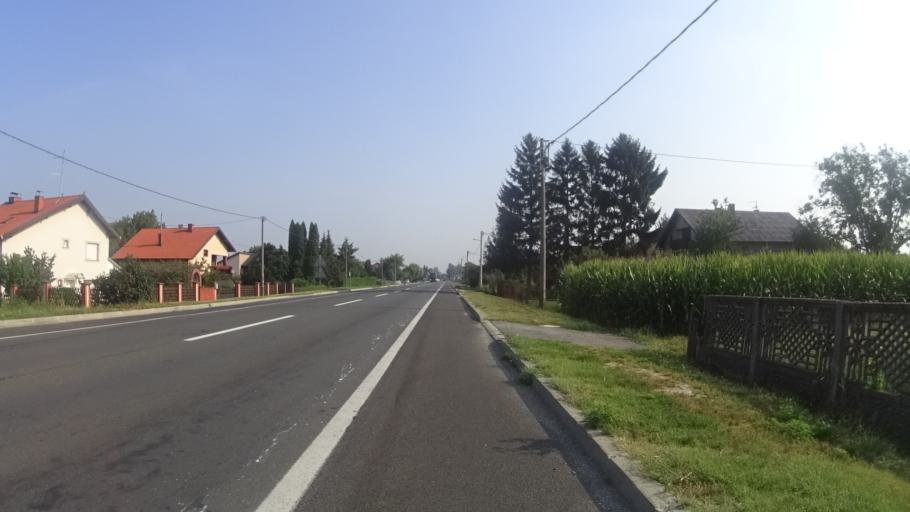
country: HR
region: Medimurska
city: Kursanec
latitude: 46.3388
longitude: 16.3615
